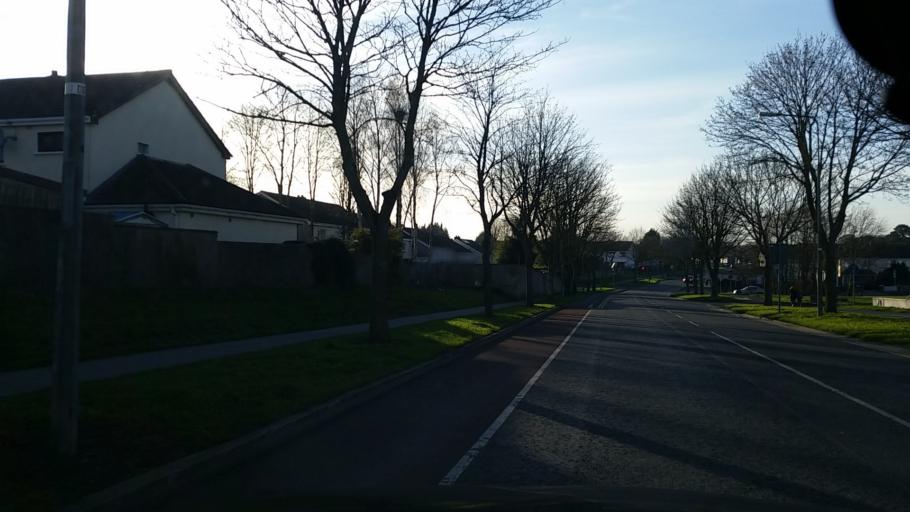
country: IE
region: Leinster
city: Hartstown
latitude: 53.4000
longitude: -6.4036
